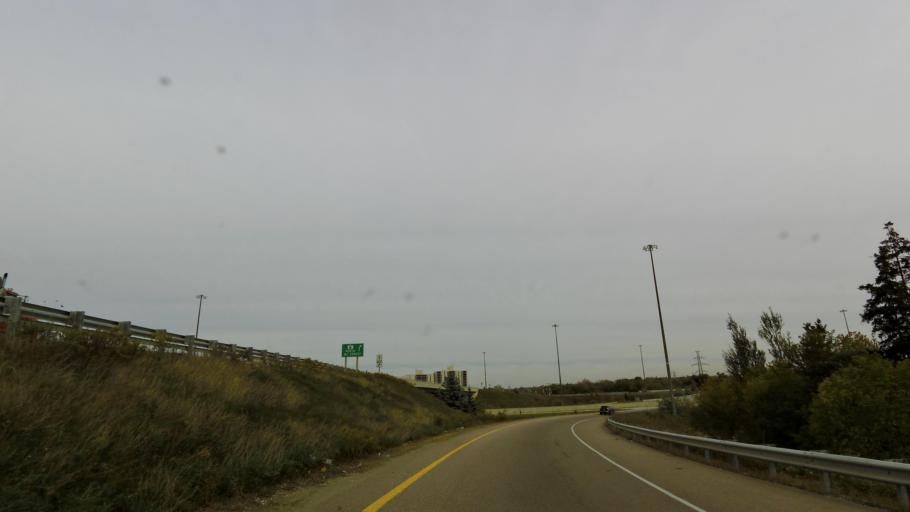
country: CA
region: Ontario
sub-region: Wellington County
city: Guelph
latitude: 43.5261
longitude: -80.2654
